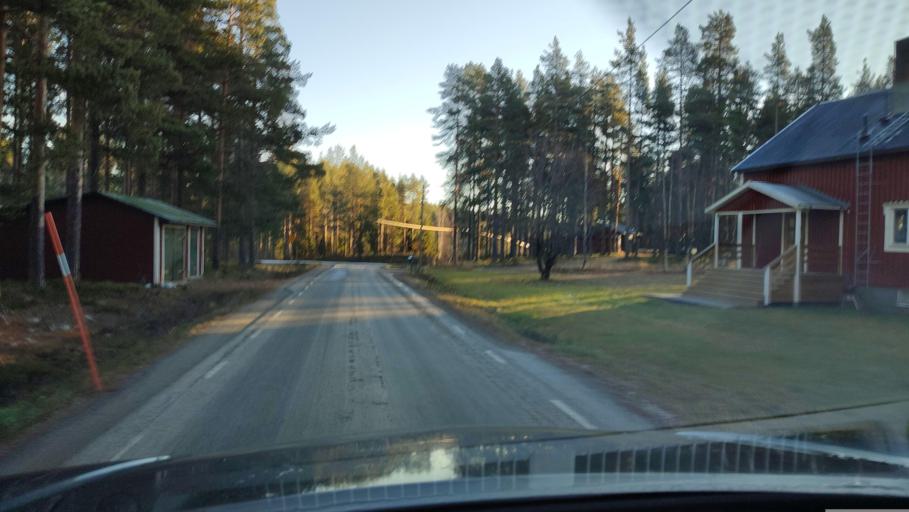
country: SE
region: Vaesterbotten
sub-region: Skelleftea Kommun
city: Viken
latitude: 64.7008
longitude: 20.9069
